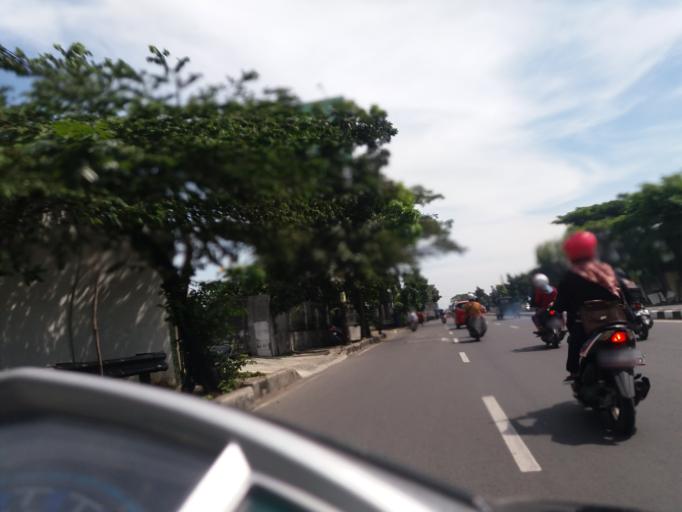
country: ID
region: West Java
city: Bandung
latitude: -6.9488
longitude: 107.6148
